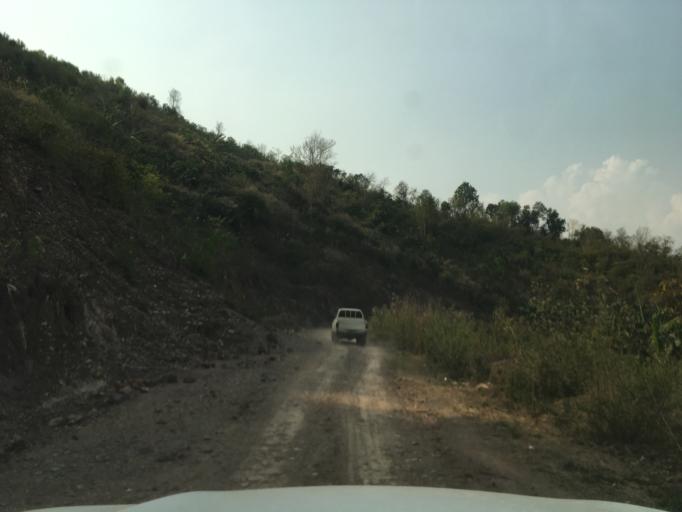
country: LA
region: Xiangkhoang
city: Phonsavan
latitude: 19.8203
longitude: 102.9944
